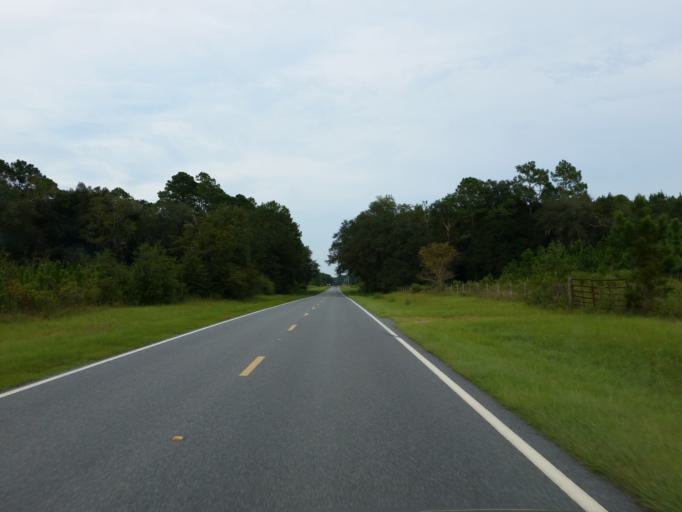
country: US
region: Georgia
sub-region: Echols County
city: Statenville
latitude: 30.5656
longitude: -83.1671
